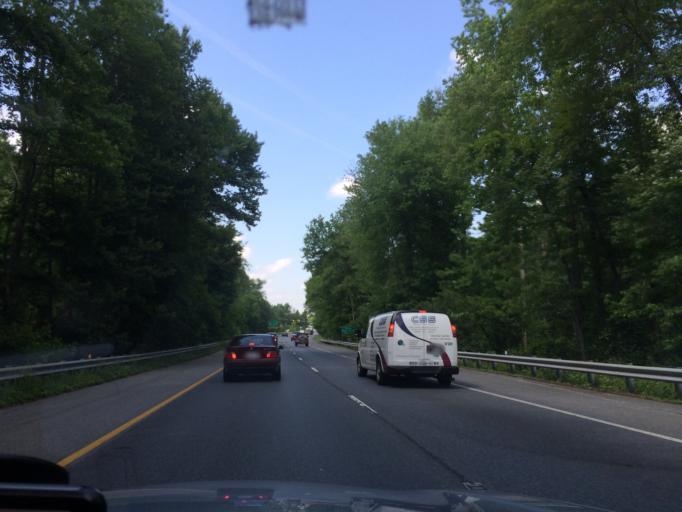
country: US
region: Maryland
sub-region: Anne Arundel County
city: Crofton
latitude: 38.9803
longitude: -76.7123
